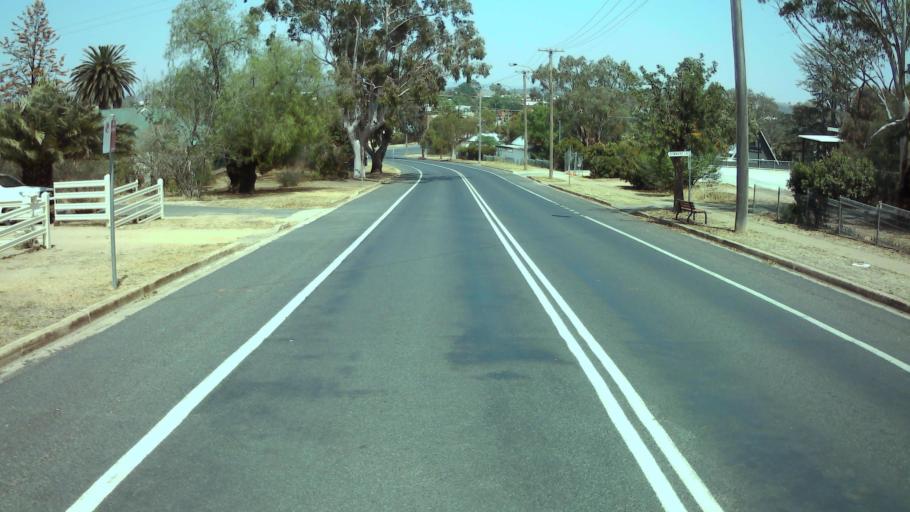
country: AU
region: New South Wales
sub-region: Weddin
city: Grenfell
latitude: -33.8951
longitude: 148.1674
